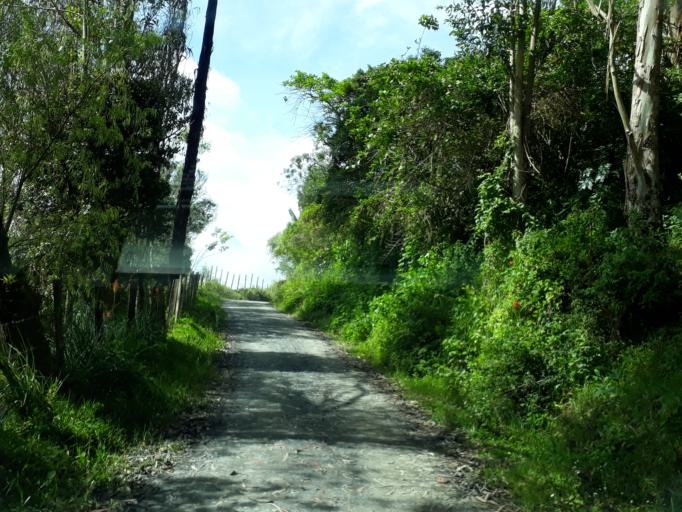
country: CO
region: Cundinamarca
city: Junin
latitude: 4.7569
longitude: -73.6316
